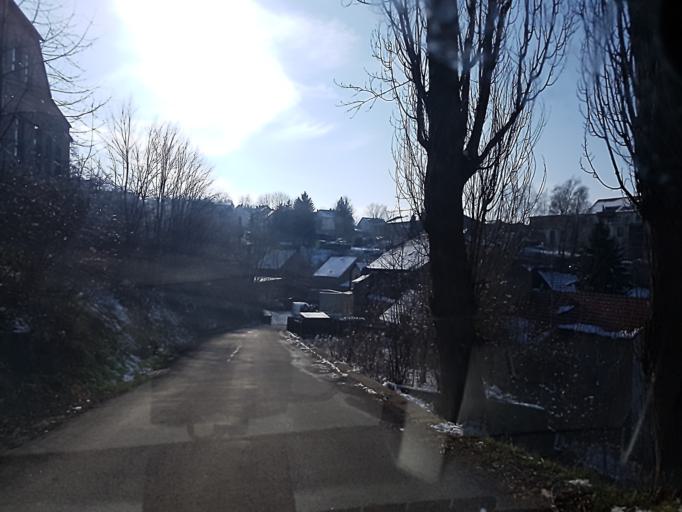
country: DE
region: Saxony
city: Leisnig
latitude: 51.1586
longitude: 12.9244
